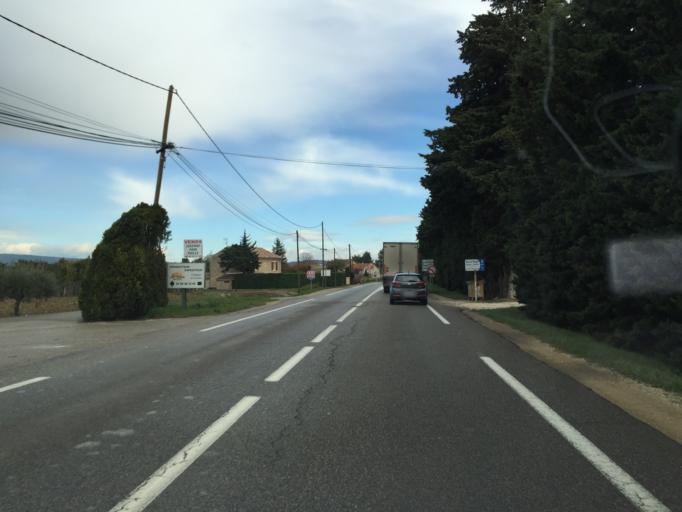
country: FR
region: Provence-Alpes-Cote d'Azur
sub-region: Departement du Vaucluse
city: Taillades
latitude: 43.8737
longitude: 5.0725
